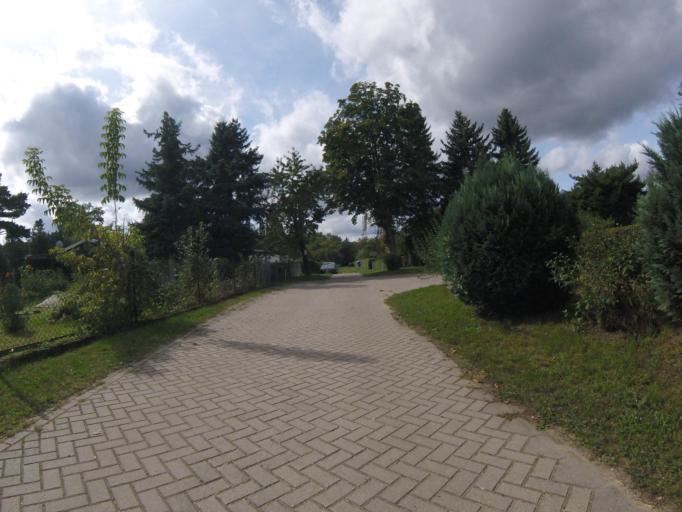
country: DE
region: Brandenburg
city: Mittenwalde
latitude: 52.2206
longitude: 13.5762
